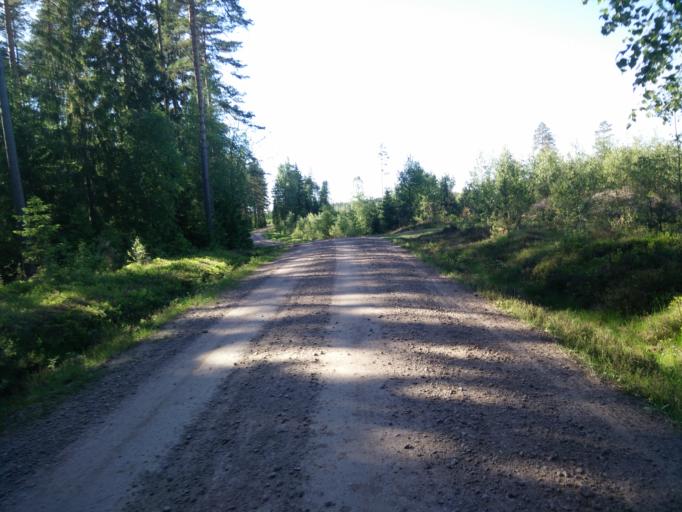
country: SE
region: Vaermland
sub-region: Hagfors Kommun
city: Hagfors
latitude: 60.0174
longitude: 13.5664
